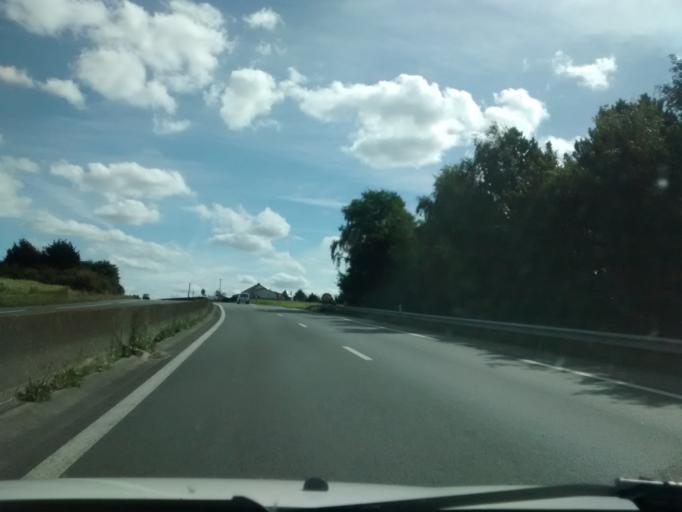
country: FR
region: Brittany
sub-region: Departement d'Ille-et-Vilaine
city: Saint-Pere
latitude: 48.5803
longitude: -1.9494
